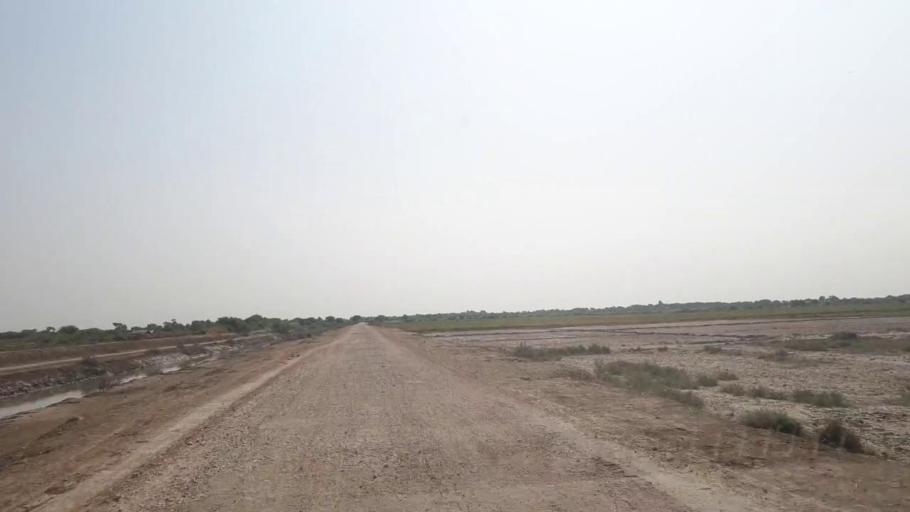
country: PK
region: Sindh
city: Kadhan
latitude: 24.4687
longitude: 68.9047
